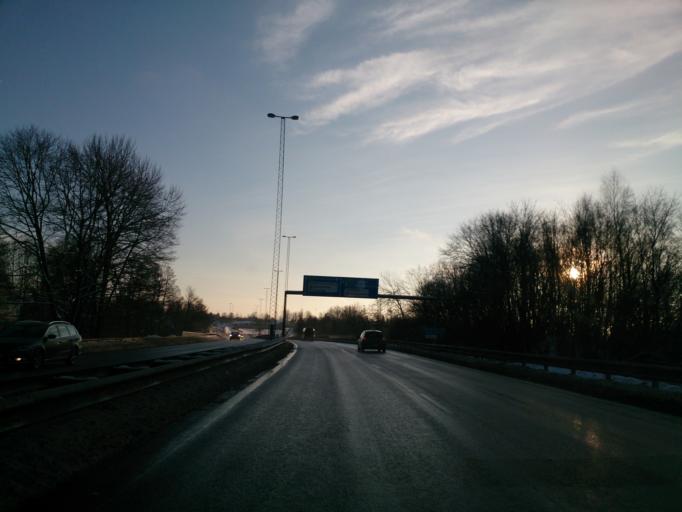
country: SE
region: OEstergoetland
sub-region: Norrkopings Kommun
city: Norrkoping
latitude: 58.5891
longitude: 16.1521
